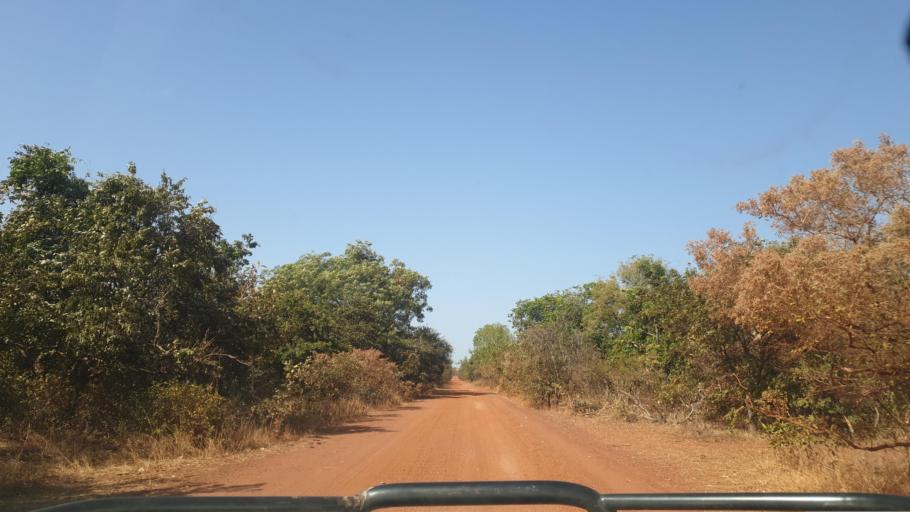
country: ML
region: Sikasso
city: Bougouni
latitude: 11.8208
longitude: -6.9535
